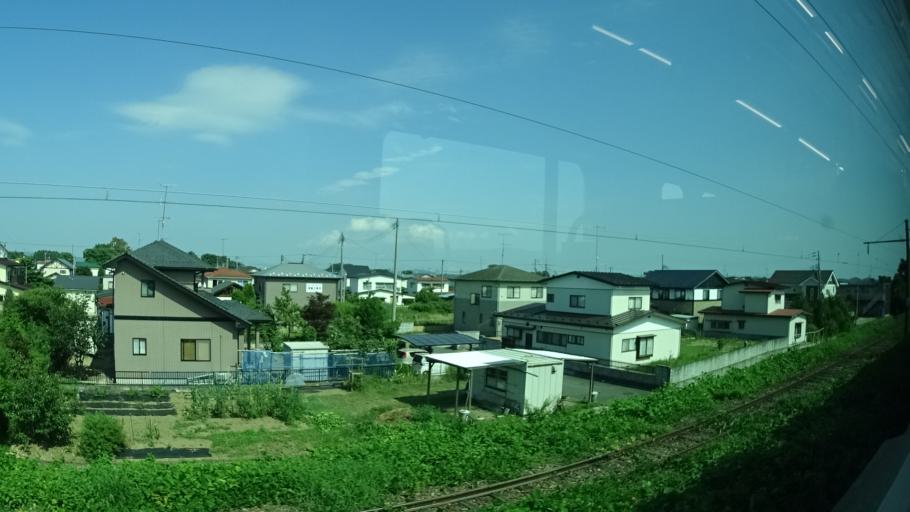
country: JP
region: Miyagi
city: Kogota
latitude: 38.5321
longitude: 141.0653
